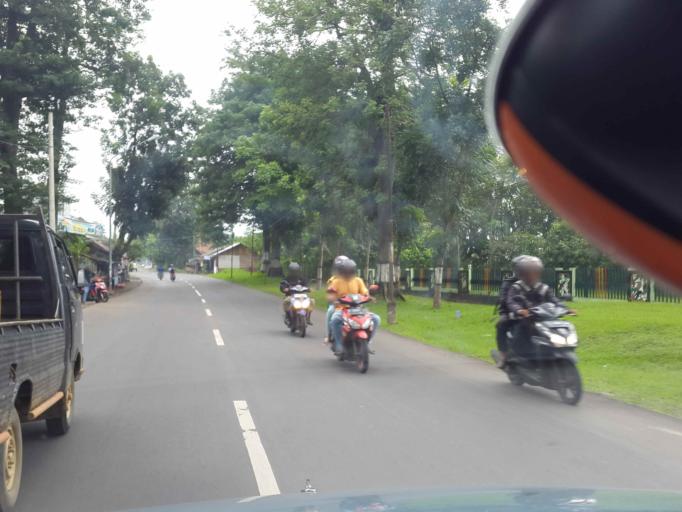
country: ID
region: Central Java
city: Wonopringgo
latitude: -6.9926
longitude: 109.6345
